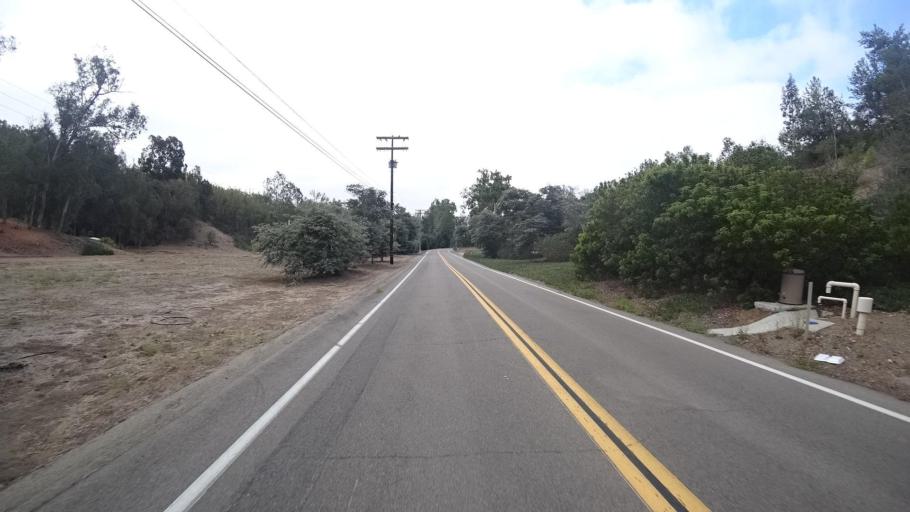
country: US
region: California
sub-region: San Diego County
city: Rancho Santa Fe
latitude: 32.9966
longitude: -117.2248
